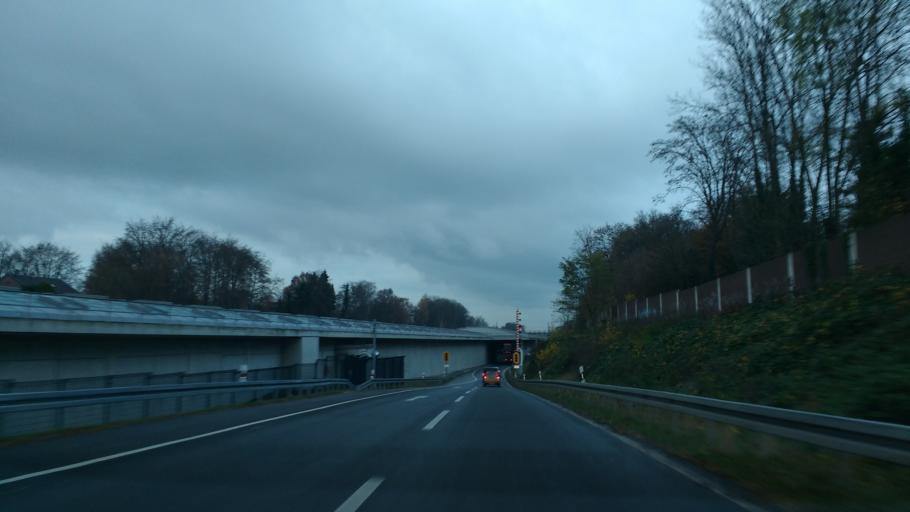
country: DE
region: North Rhine-Westphalia
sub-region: Regierungsbezirk Koln
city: Mengenich
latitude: 50.9391
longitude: 6.8500
